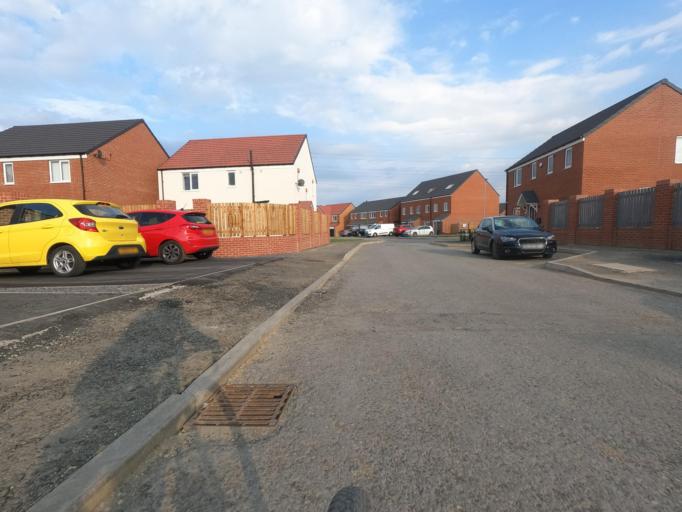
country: GB
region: England
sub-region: Northumberland
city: Cramlington
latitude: 55.0848
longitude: -1.6221
